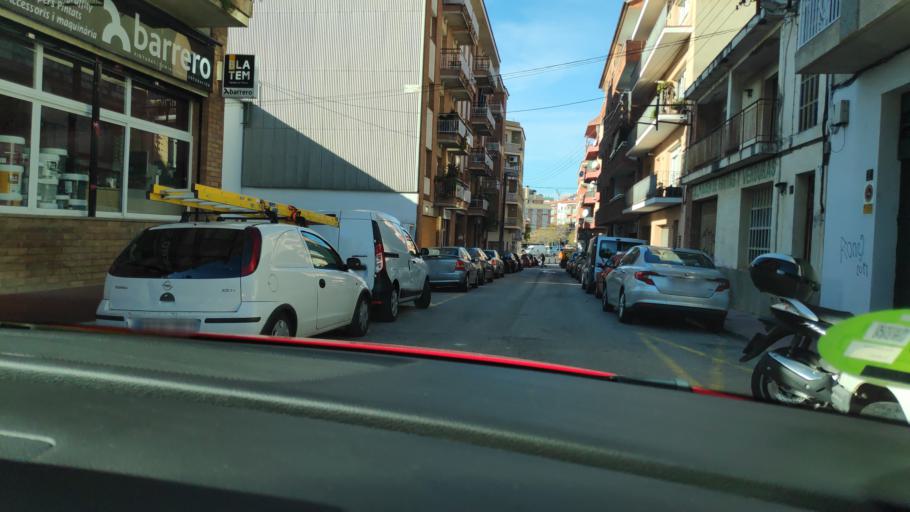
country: ES
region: Catalonia
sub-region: Provincia de Girona
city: Lloret de Mar
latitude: 41.7070
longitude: 2.8416
